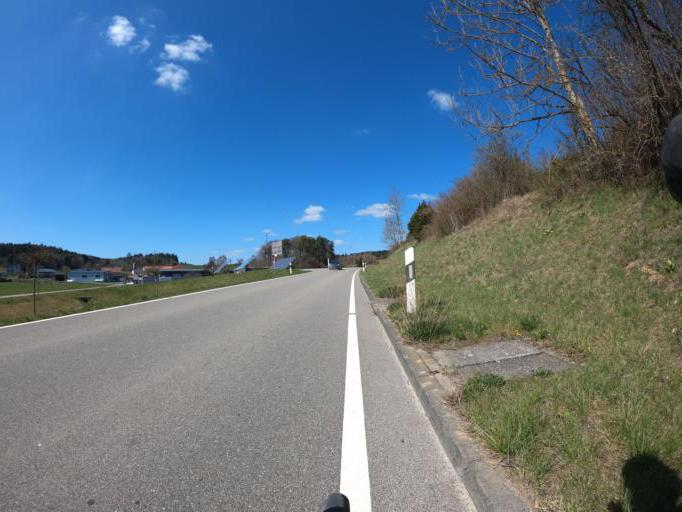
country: DE
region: Baden-Wuerttemberg
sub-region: Karlsruhe Region
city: Empfingen
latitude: 48.4232
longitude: 8.7489
